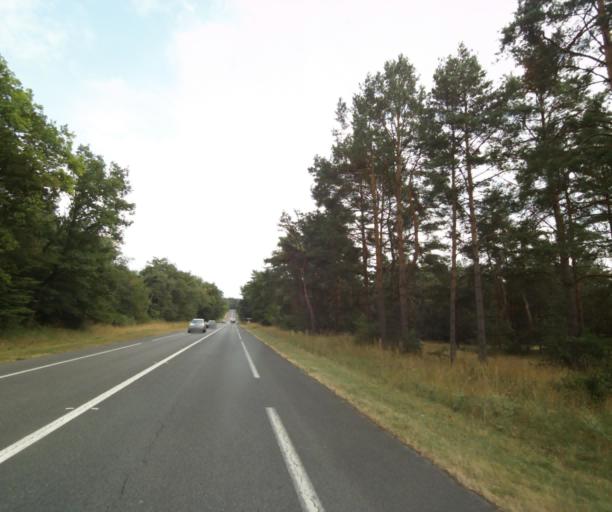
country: FR
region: Ile-de-France
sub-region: Departement de Seine-et-Marne
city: Fontainebleau
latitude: 48.4362
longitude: 2.6936
